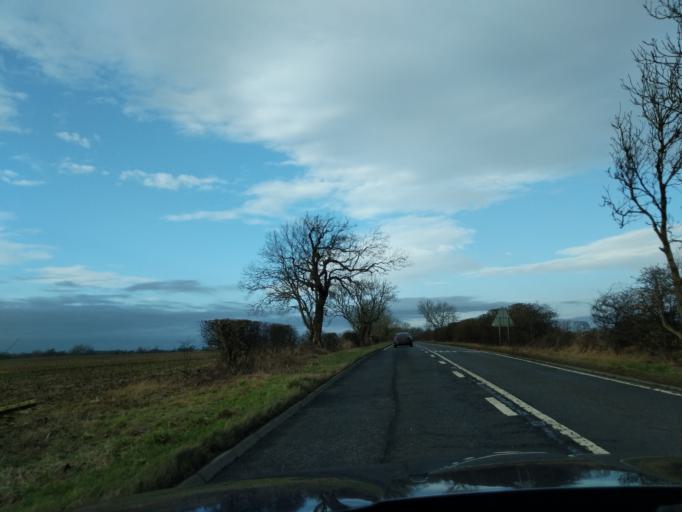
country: GB
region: England
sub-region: Northumberland
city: Darras Hall
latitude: 55.0656
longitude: -1.7829
